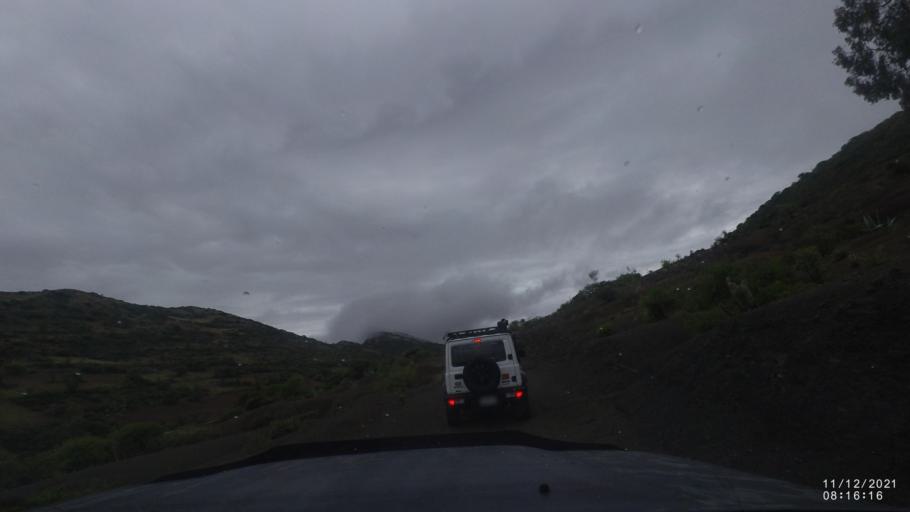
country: BO
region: Cochabamba
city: Tarata
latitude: -17.9440
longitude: -65.9283
